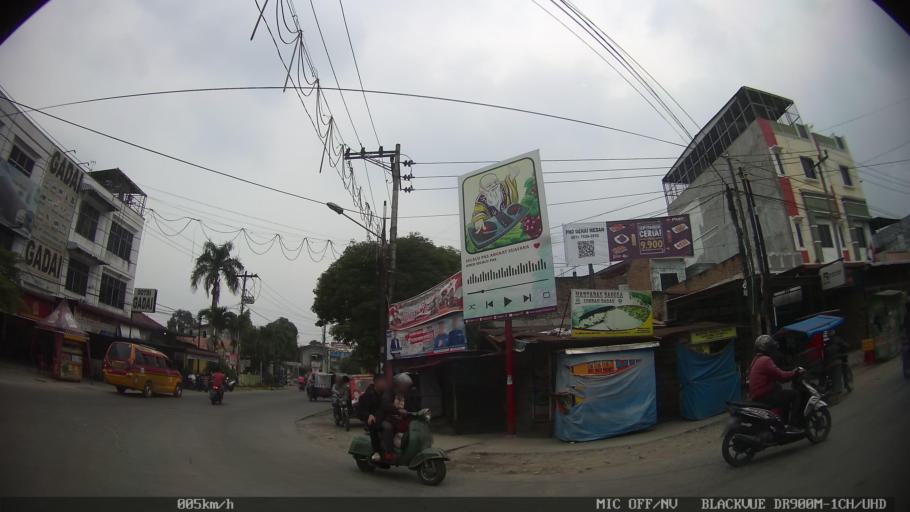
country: ID
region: North Sumatra
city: Medan
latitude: 3.5808
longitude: 98.7294
